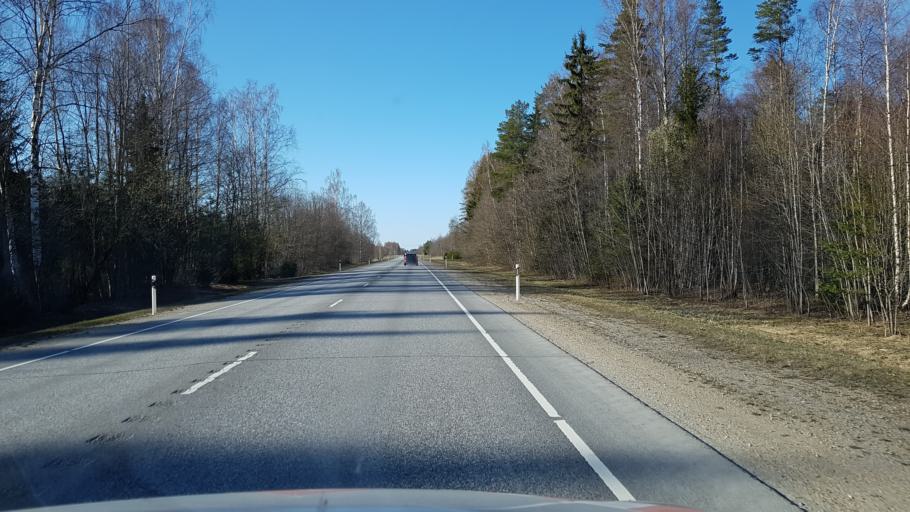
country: EE
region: Ida-Virumaa
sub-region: Johvi vald
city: Johvi
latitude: 59.2055
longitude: 27.3442
